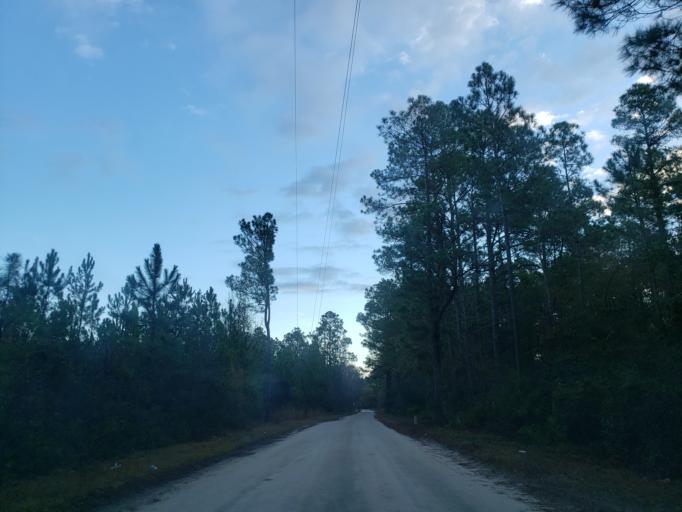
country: US
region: Georgia
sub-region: Chatham County
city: Bloomingdale
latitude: 32.1170
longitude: -81.3422
